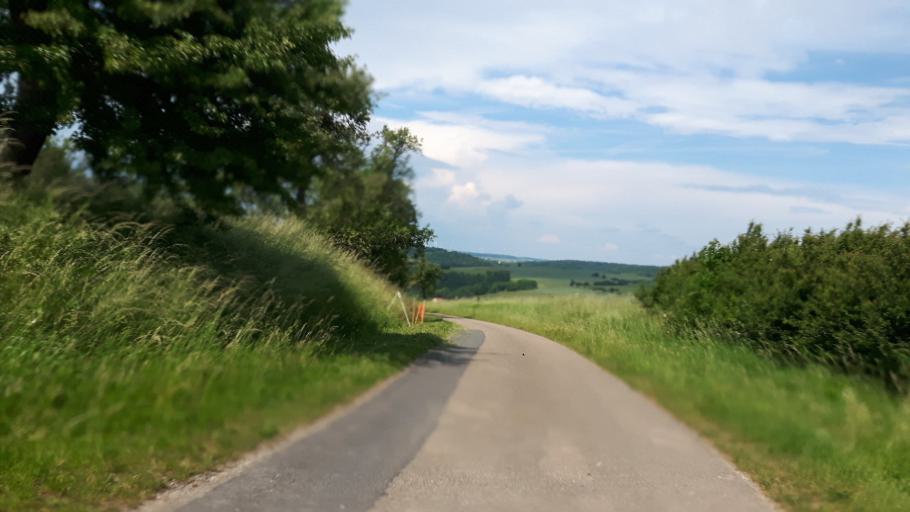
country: DE
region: Baden-Wuerttemberg
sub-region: Regierungsbezirk Stuttgart
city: Forchtenberg
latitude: 49.3354
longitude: 9.5280
